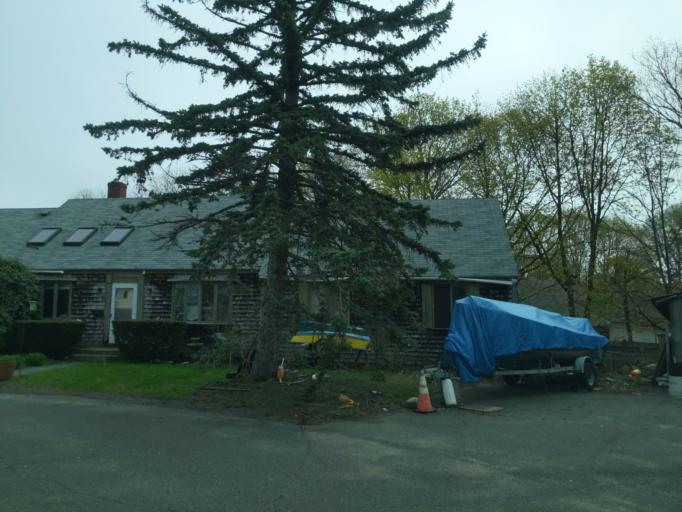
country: US
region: Massachusetts
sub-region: Essex County
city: Rockport
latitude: 42.6537
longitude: -70.6056
